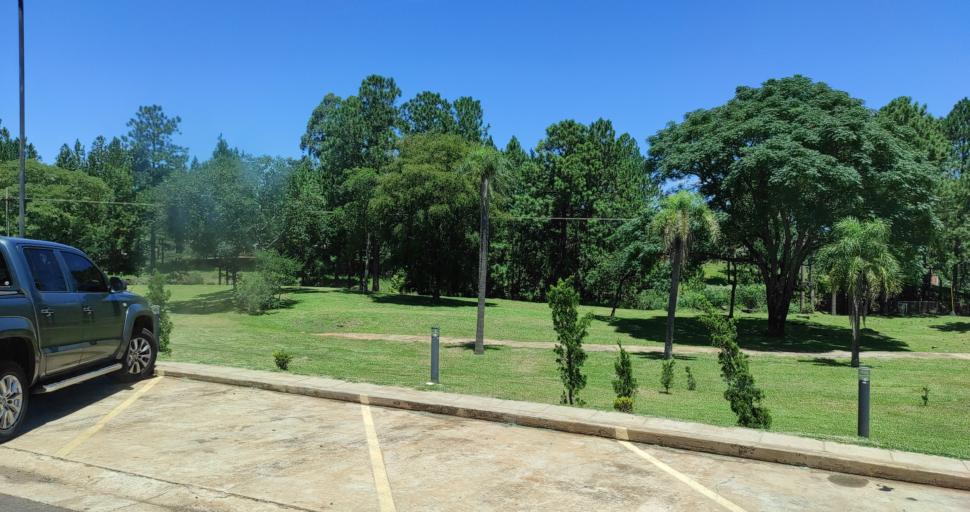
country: AR
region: Misiones
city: Dos de Mayo
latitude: -27.0435
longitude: -54.6839
